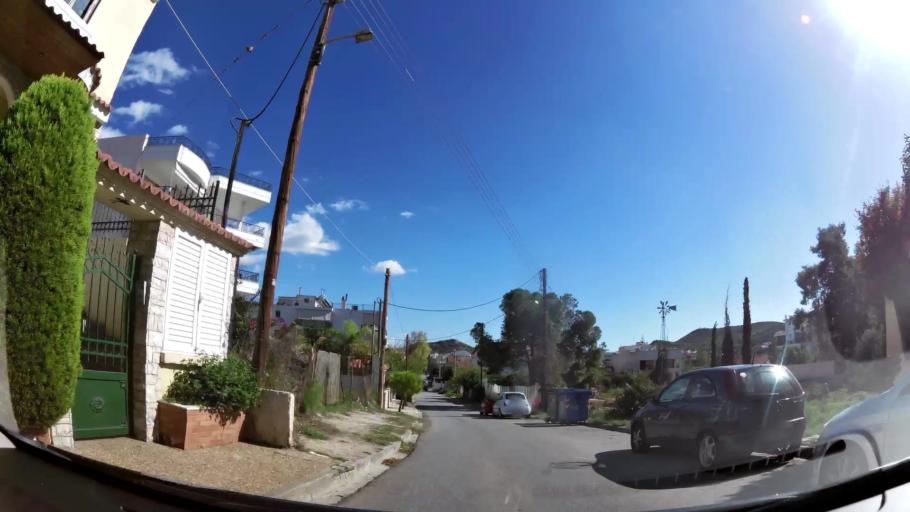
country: GR
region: Attica
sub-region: Nomarchia Anatolikis Attikis
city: Voula
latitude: 37.8378
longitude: 23.7793
